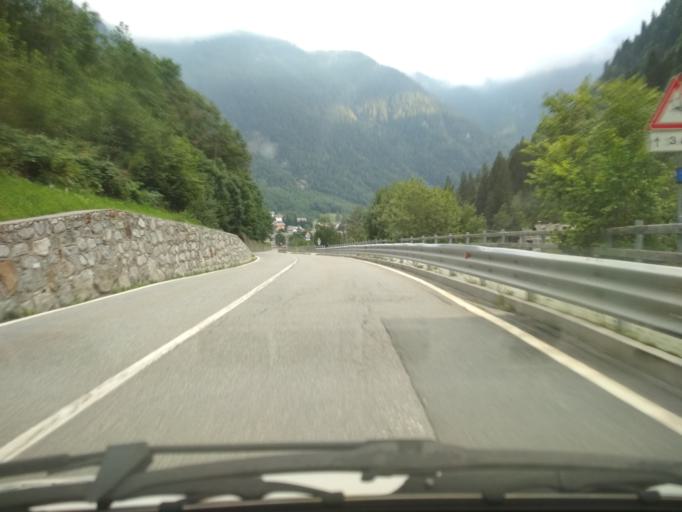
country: IT
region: Aosta Valley
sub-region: Valle d'Aosta
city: Gaby
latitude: 45.7204
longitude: 7.8764
